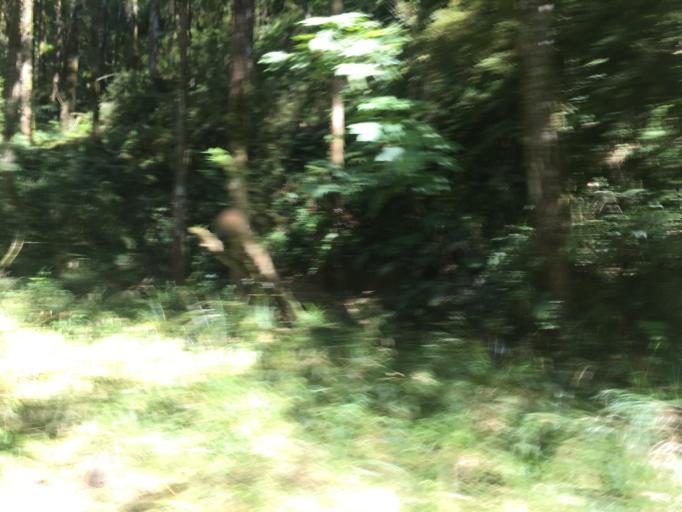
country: TW
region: Taiwan
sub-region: Yilan
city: Yilan
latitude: 24.6181
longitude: 121.4690
